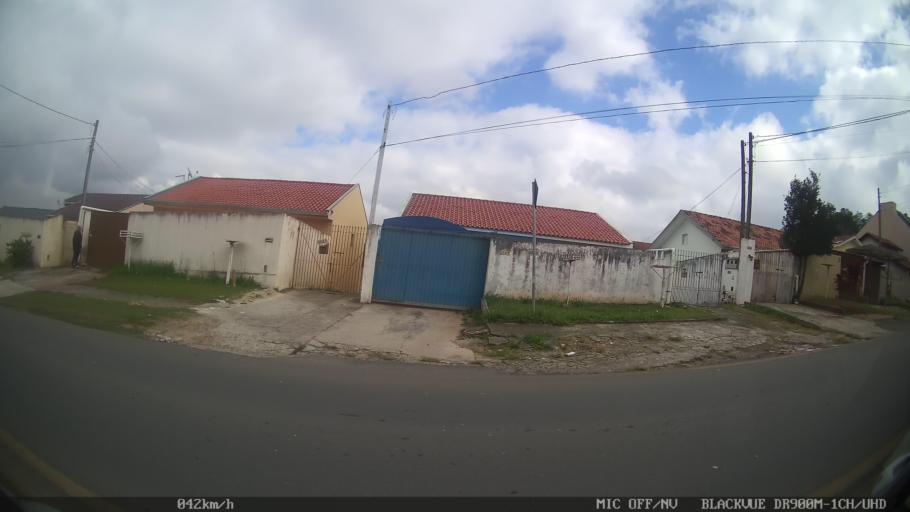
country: BR
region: Parana
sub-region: Curitiba
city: Curitiba
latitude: -25.3664
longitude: -49.2503
